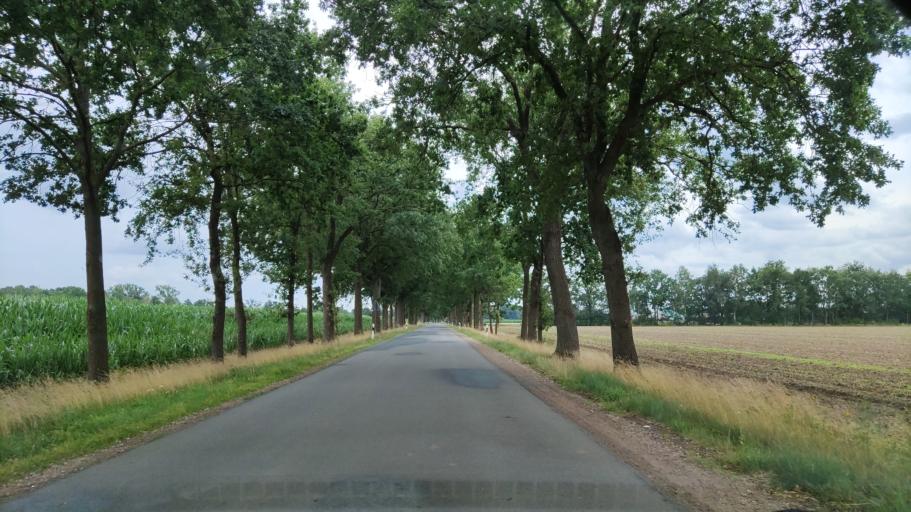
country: DE
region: Lower Saxony
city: Dannenberg
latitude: 53.0731
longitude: 11.1272
